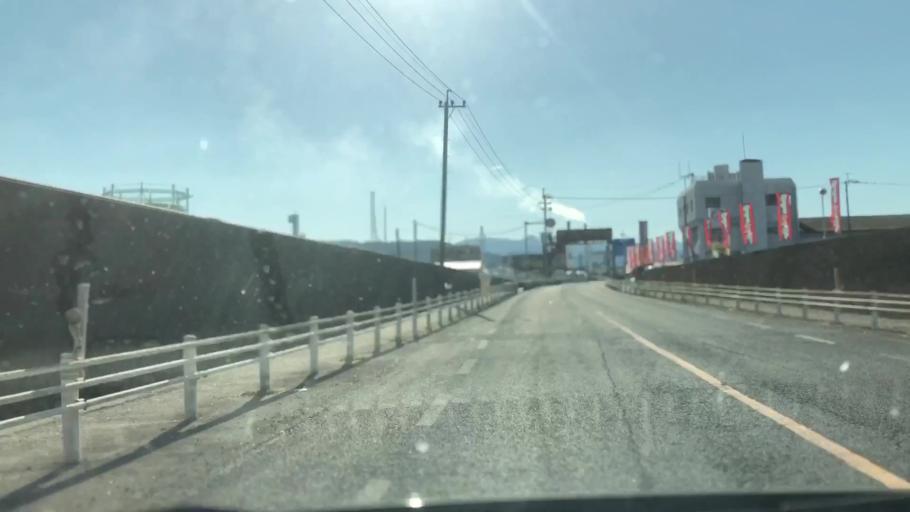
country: JP
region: Kagoshima
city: Satsumasendai
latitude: 31.8276
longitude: 130.3040
